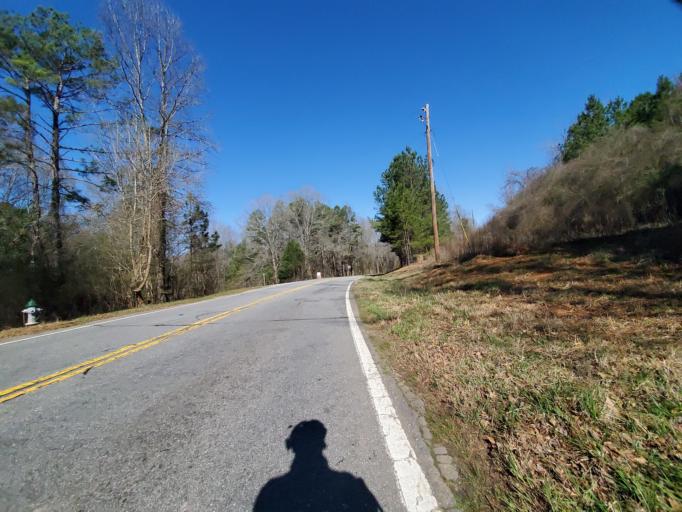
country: US
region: Georgia
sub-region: Oconee County
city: Bogart
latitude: 33.9969
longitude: -83.4950
